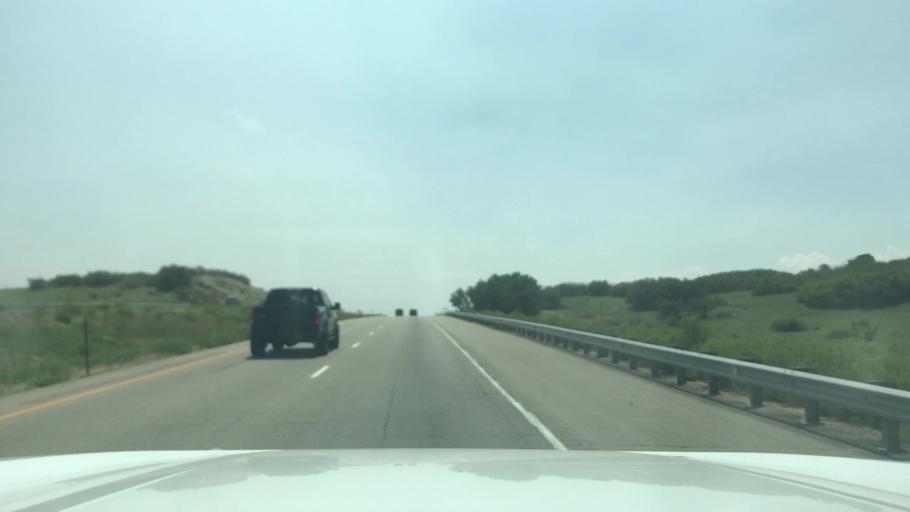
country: US
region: Colorado
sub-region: Pueblo County
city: Colorado City
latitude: 37.9016
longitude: -104.8292
